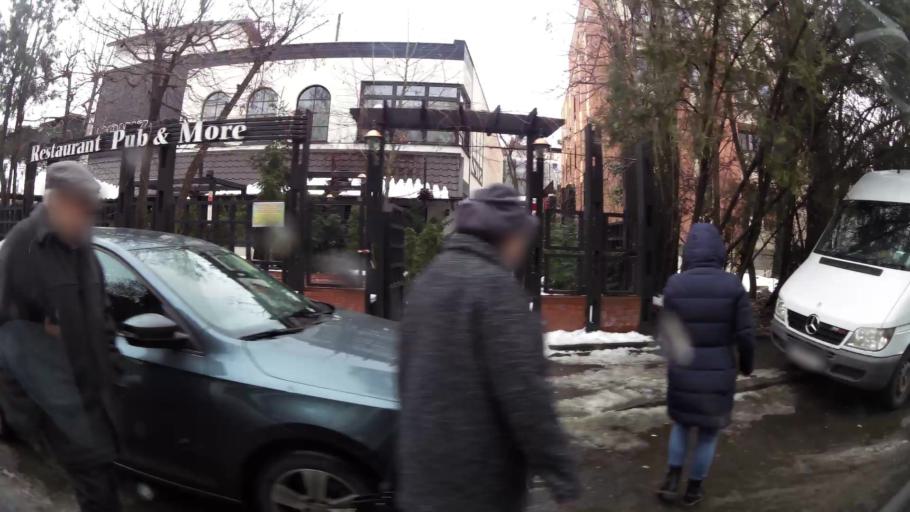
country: RO
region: Ilfov
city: Dobroesti
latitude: 44.4213
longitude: 26.1701
